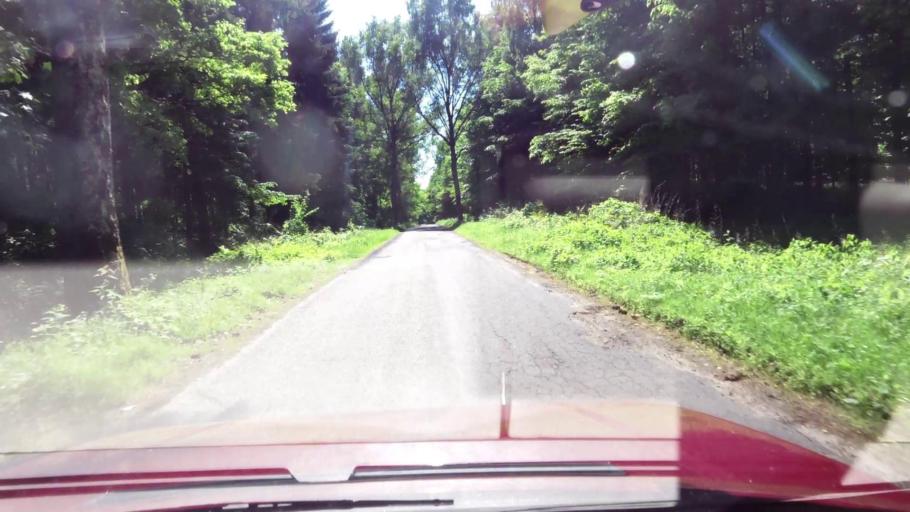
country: PL
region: West Pomeranian Voivodeship
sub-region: Powiat koszalinski
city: Bobolice
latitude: 54.0271
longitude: 16.6401
